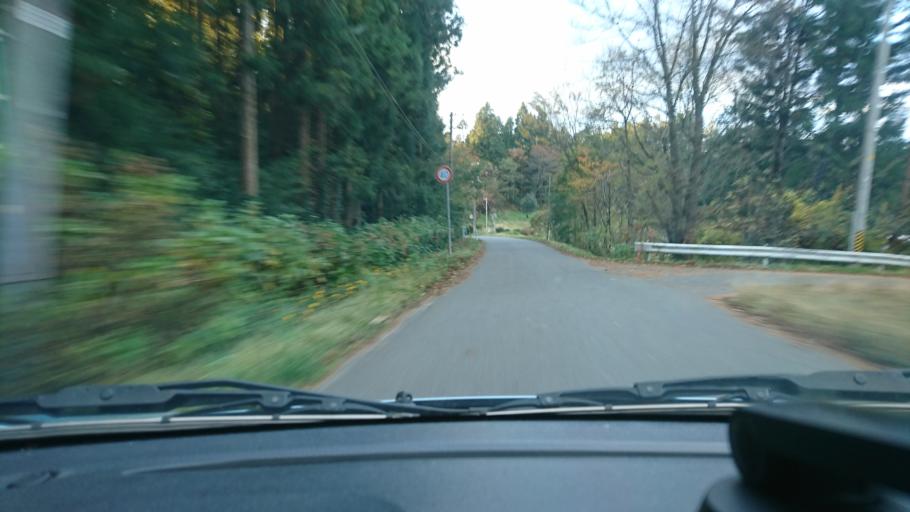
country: JP
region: Iwate
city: Ichinoseki
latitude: 38.7907
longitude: 141.1851
